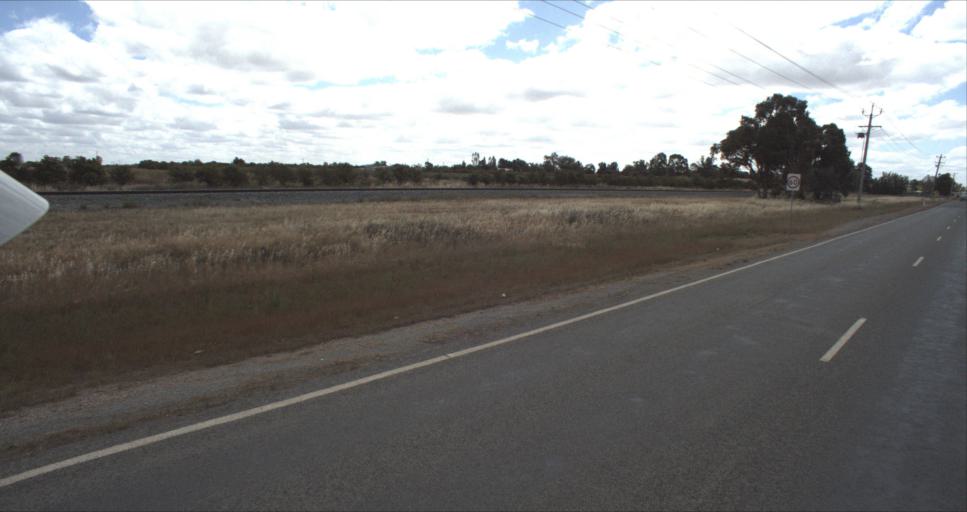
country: AU
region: New South Wales
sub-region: Leeton
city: Leeton
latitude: -34.5734
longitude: 146.3948
